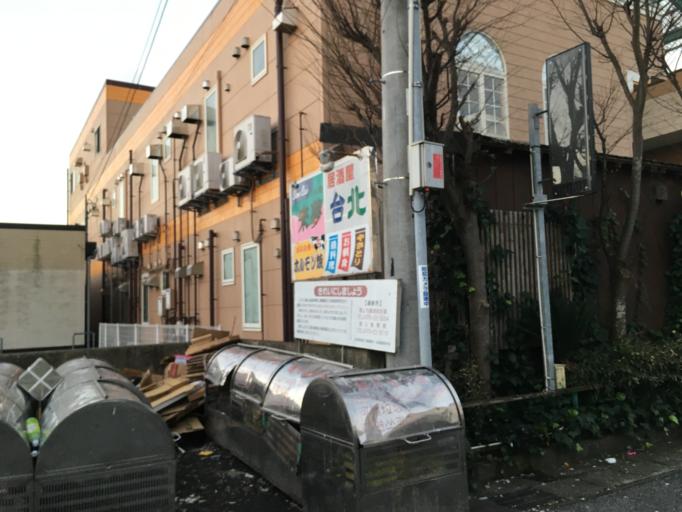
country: JP
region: Chiba
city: Tateyama
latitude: 34.9946
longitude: 139.8600
